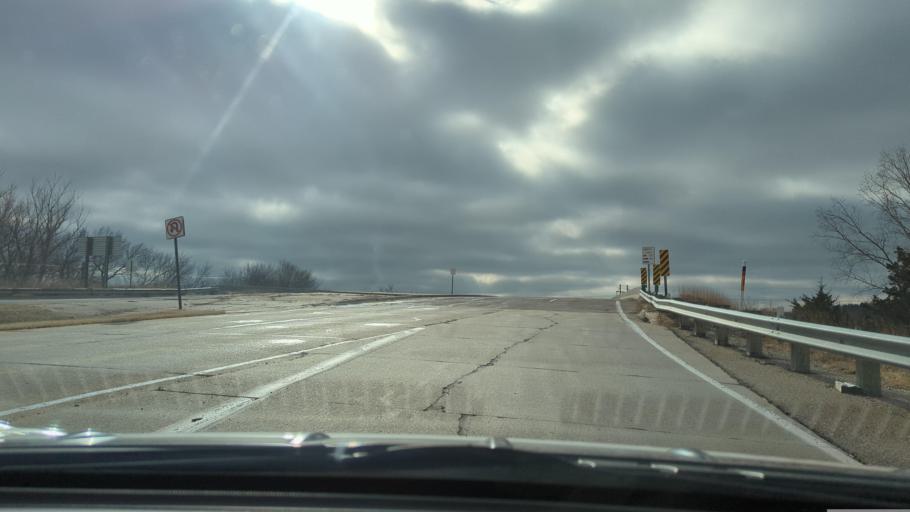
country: US
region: Nebraska
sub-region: Sarpy County
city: Offutt Air Force Base
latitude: 41.1133
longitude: -95.9274
